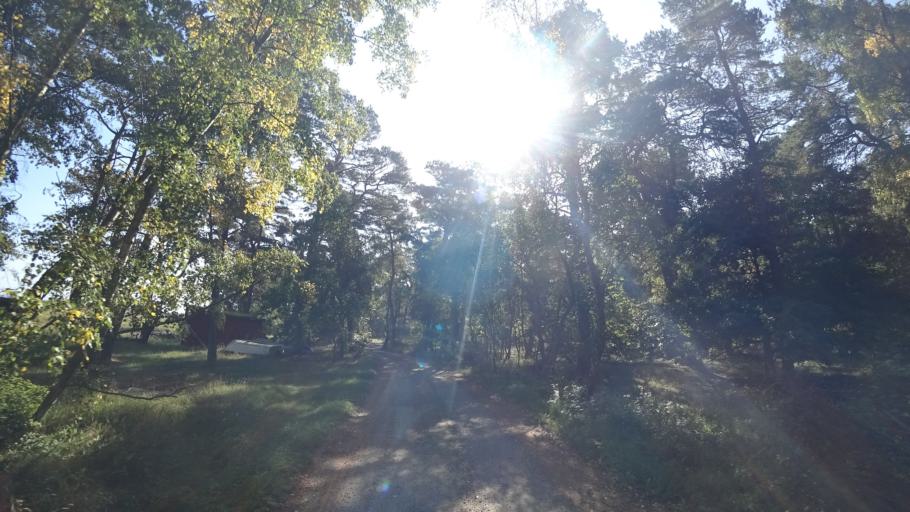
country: SE
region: Skane
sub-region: Kristianstads Kommun
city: Ahus
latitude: 55.9260
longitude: 14.3184
